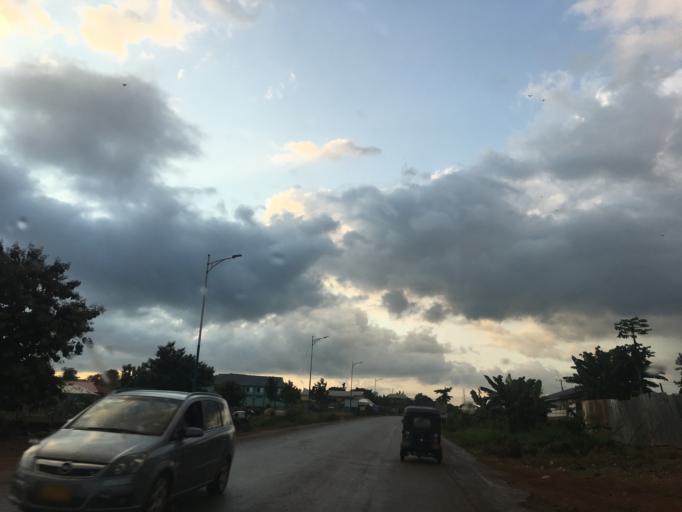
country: GH
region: Western
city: Bibiani
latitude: 6.7816
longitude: -2.5154
